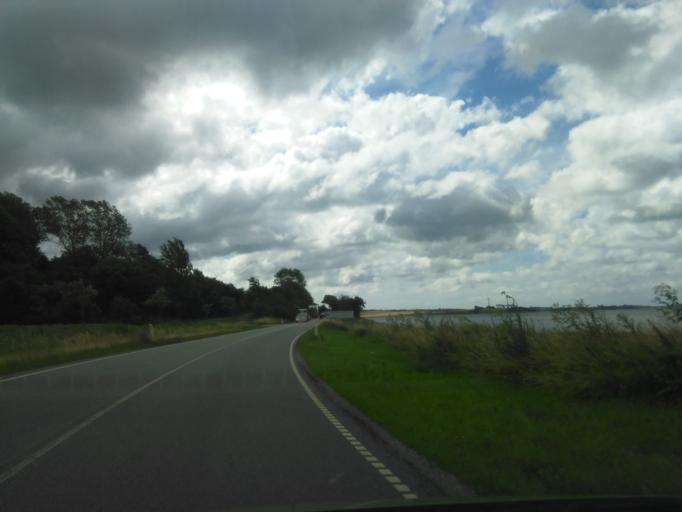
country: DK
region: Central Jutland
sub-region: Syddjurs Kommune
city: Ronde
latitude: 56.2818
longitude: 10.4866
